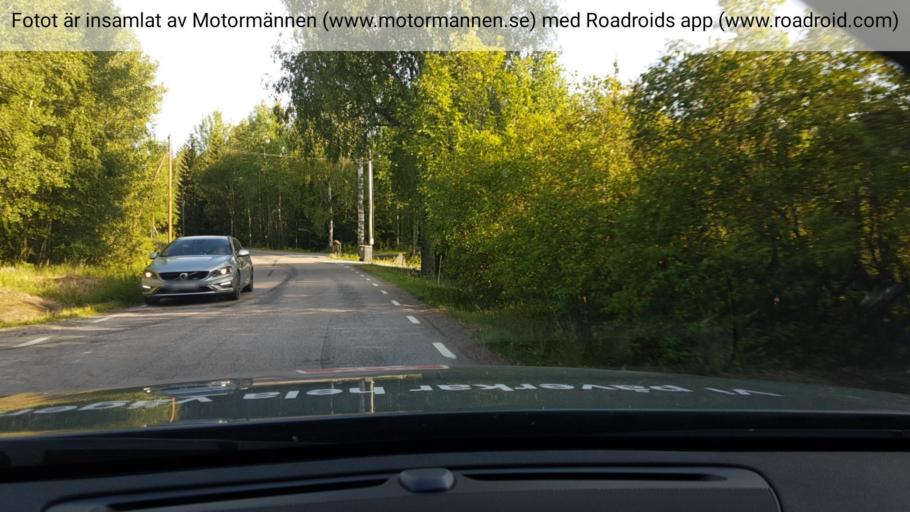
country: SE
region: Uppsala
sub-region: Osthammars Kommun
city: Gimo
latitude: 59.9770
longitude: 18.0619
